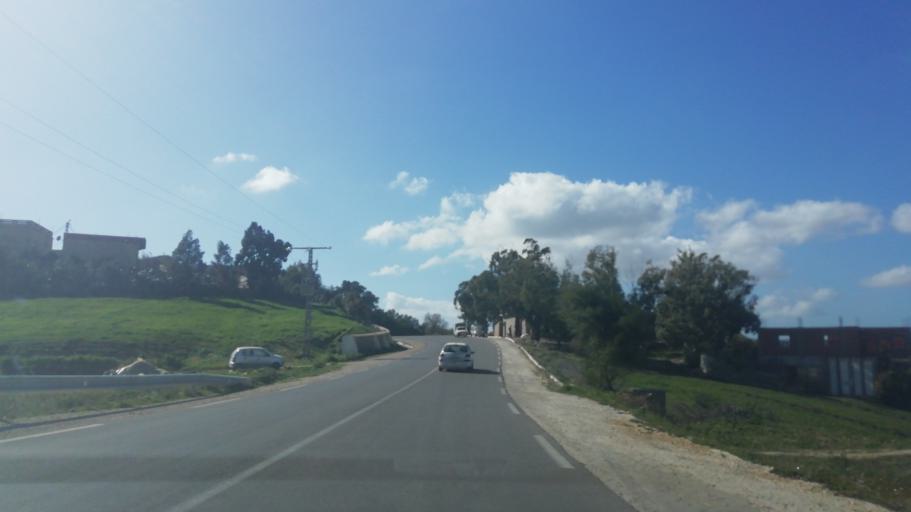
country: DZ
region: Relizane
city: Relizane
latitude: 36.0858
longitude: 0.5081
